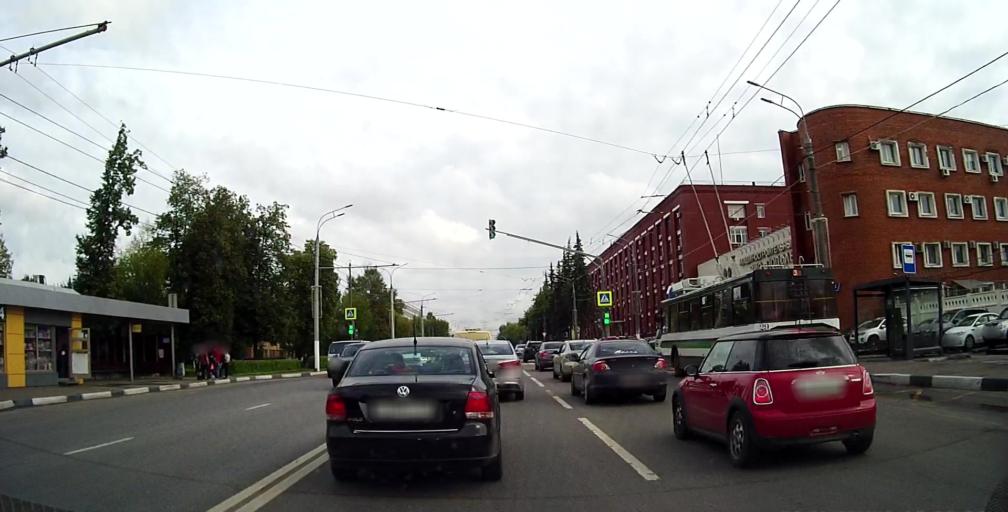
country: RU
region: Moskovskaya
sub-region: Podol'skiy Rayon
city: Podol'sk
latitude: 55.4198
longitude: 37.5701
